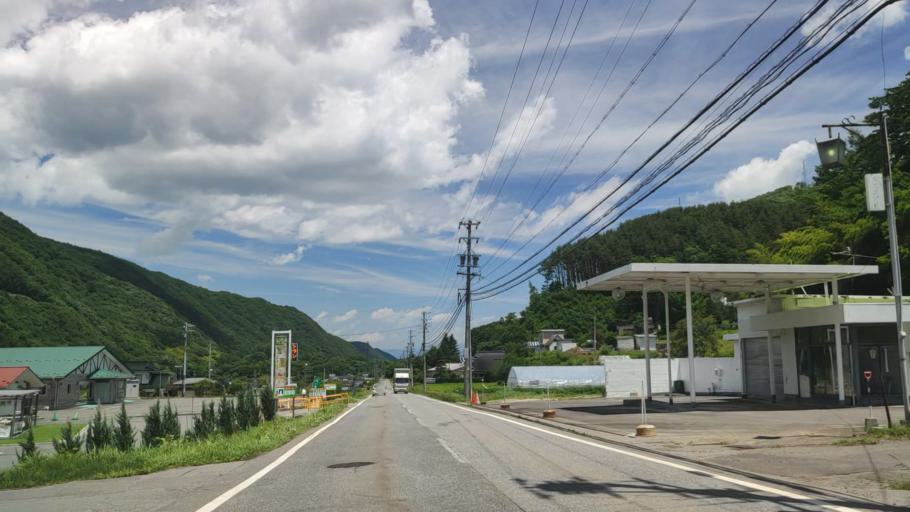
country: JP
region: Nagano
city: Kamimaruko
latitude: 36.2016
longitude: 138.2437
